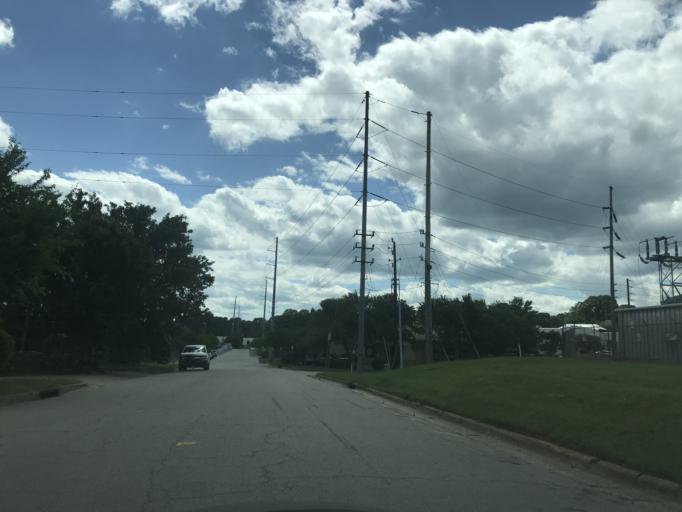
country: US
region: North Carolina
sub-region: Wake County
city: Raleigh
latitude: 35.8042
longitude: -78.6312
